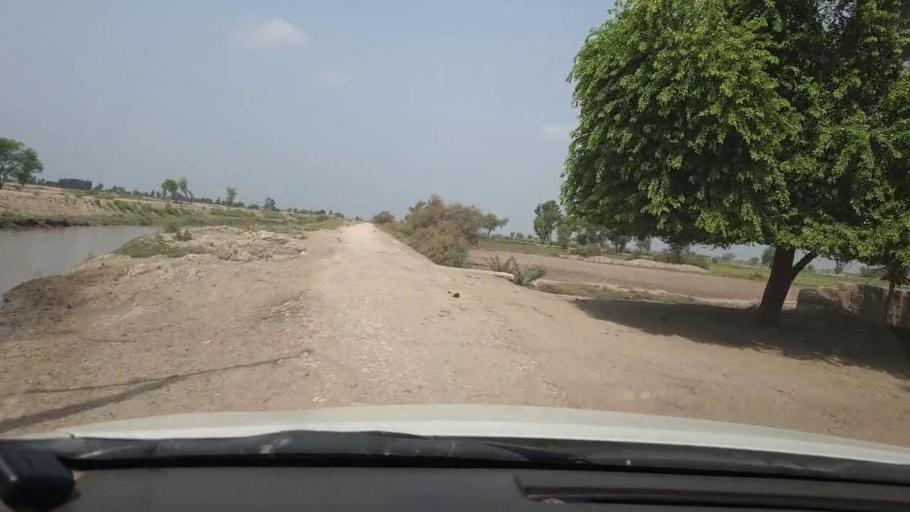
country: PK
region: Sindh
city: Garhi Yasin
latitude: 28.0130
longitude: 68.5329
